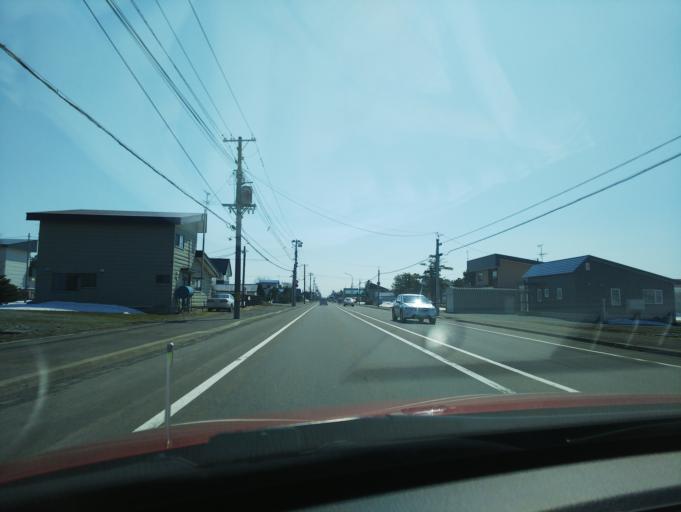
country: JP
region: Hokkaido
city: Nayoro
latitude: 44.2457
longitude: 142.3947
